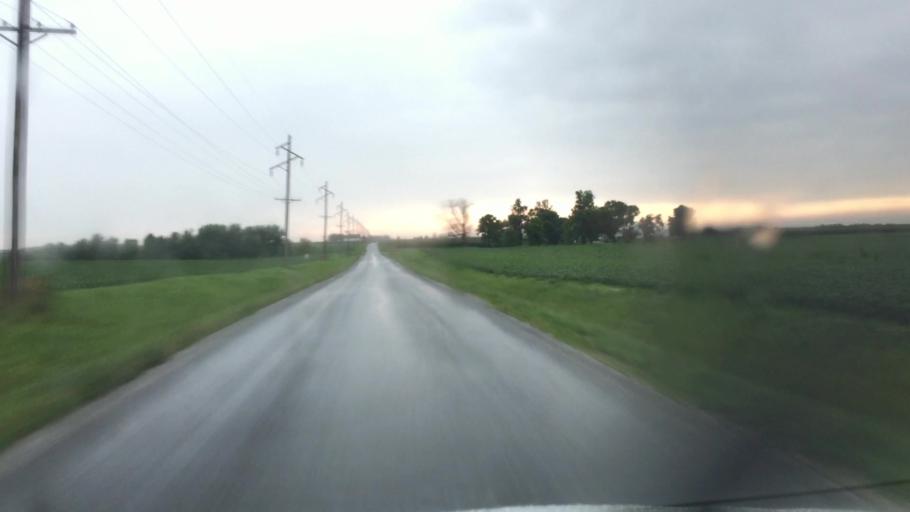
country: US
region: Illinois
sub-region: Hancock County
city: Nauvoo
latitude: 40.5032
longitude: -91.2698
